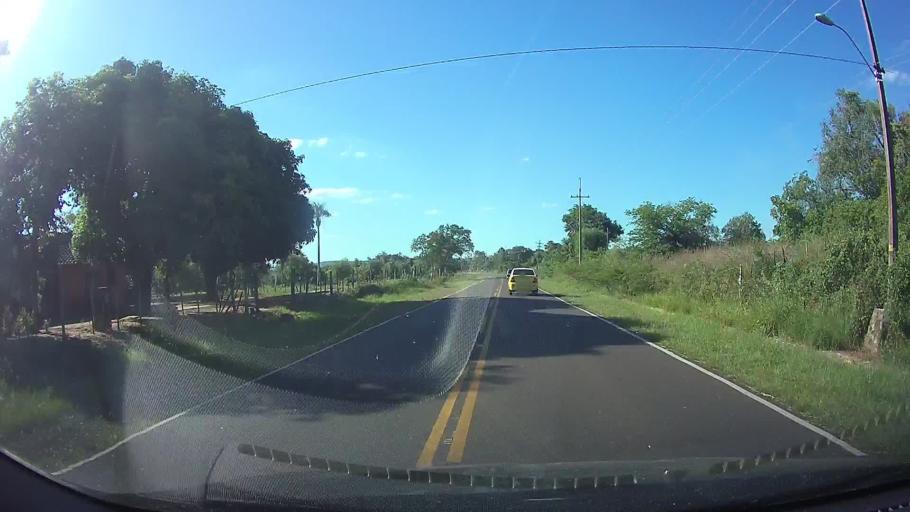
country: PY
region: Cordillera
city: Atyra
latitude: -25.2974
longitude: -57.1625
